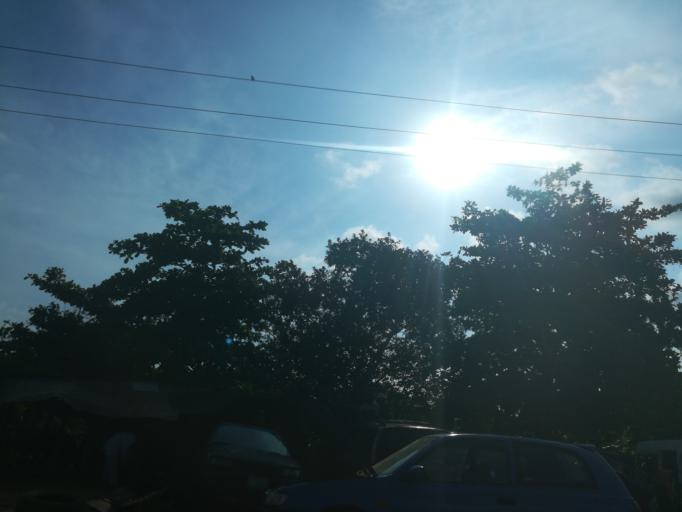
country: NG
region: Ogun
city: Ado Odo
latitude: 6.4992
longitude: 3.0851
